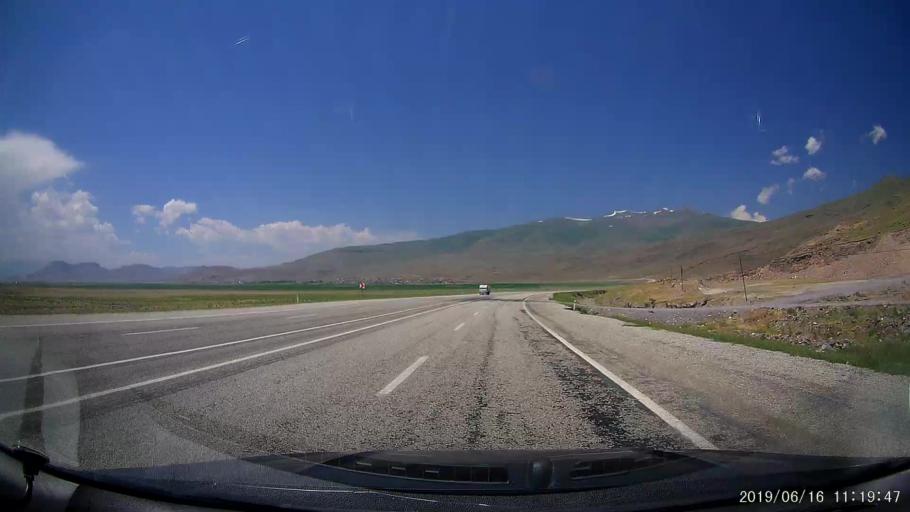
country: TR
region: Agri
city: Dogubayazit
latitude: 39.6959
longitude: 44.1070
